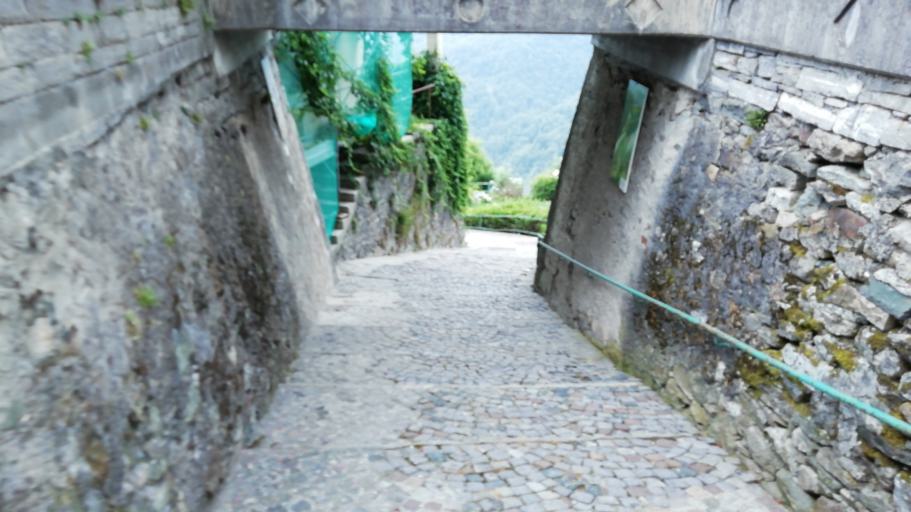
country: IT
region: Piedmont
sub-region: Provincia Verbano-Cusio-Ossola
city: San Lorenzo
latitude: 46.1270
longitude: 8.2012
